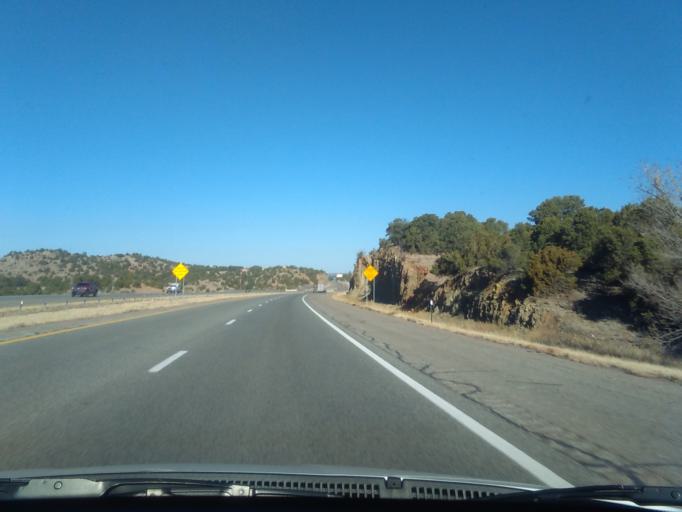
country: US
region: New Mexico
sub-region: Santa Fe County
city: Santa Fe
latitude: 35.6161
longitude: -105.9179
